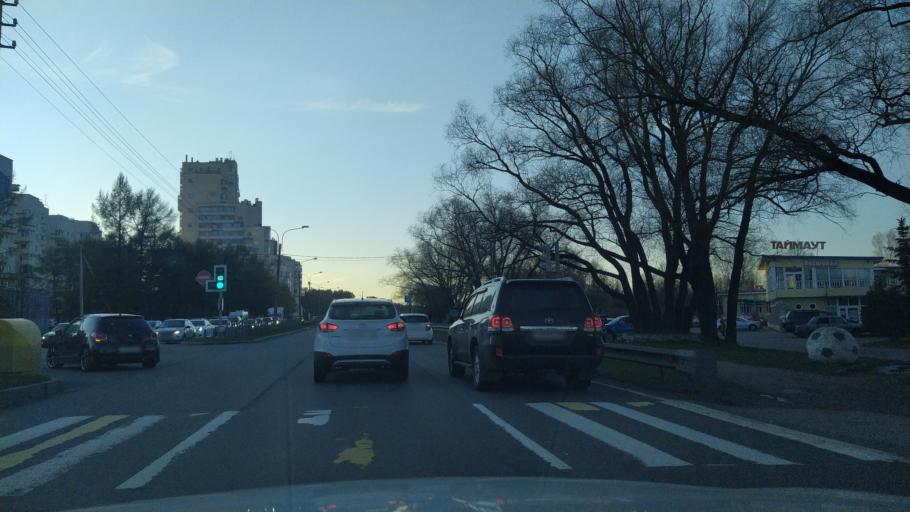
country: RU
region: St.-Petersburg
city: Sestroretsk
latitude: 60.1039
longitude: 29.9771
